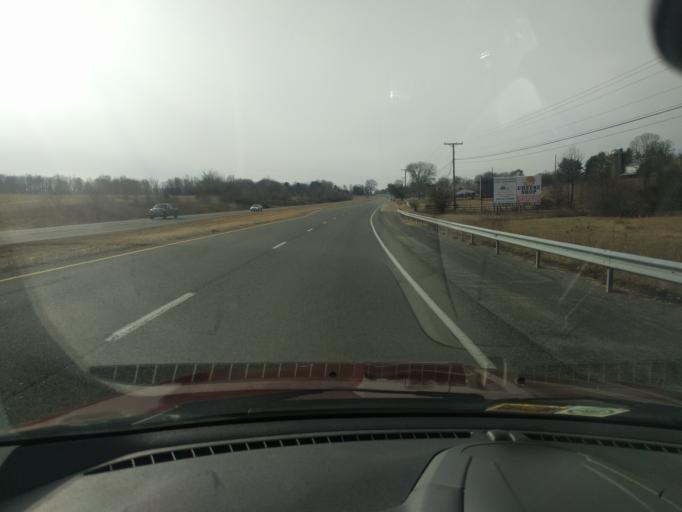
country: US
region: Virginia
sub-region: Augusta County
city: Lyndhurst
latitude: 38.0520
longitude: -78.9654
